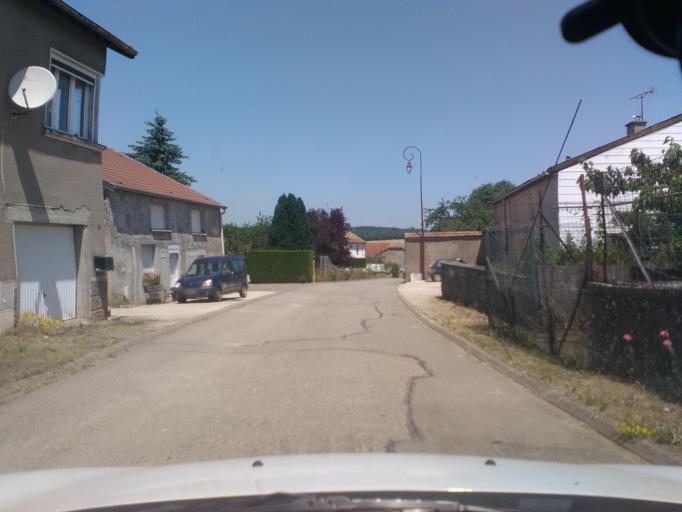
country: FR
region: Lorraine
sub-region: Departement de la Meuse
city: Gondrecourt-le-Chateau
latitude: 48.4221
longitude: 5.5265
